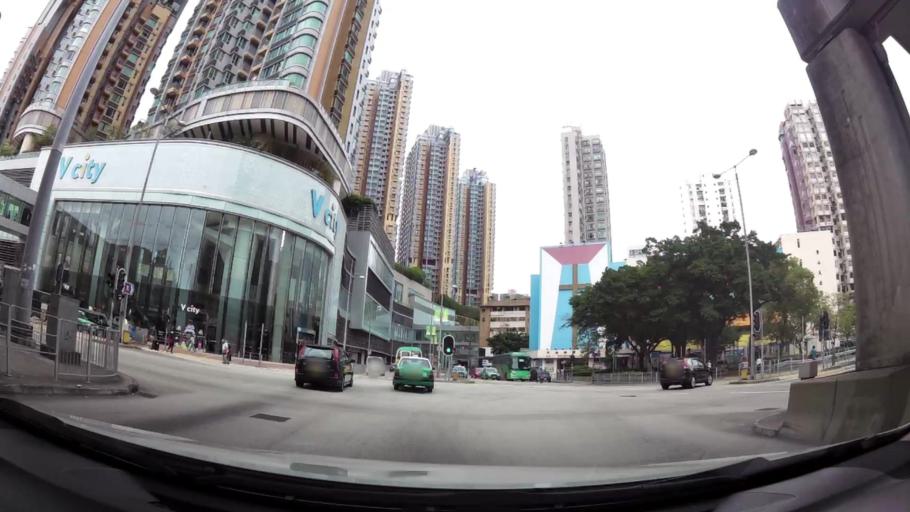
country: HK
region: Tuen Mun
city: Tuen Mun
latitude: 22.3941
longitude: 113.9748
